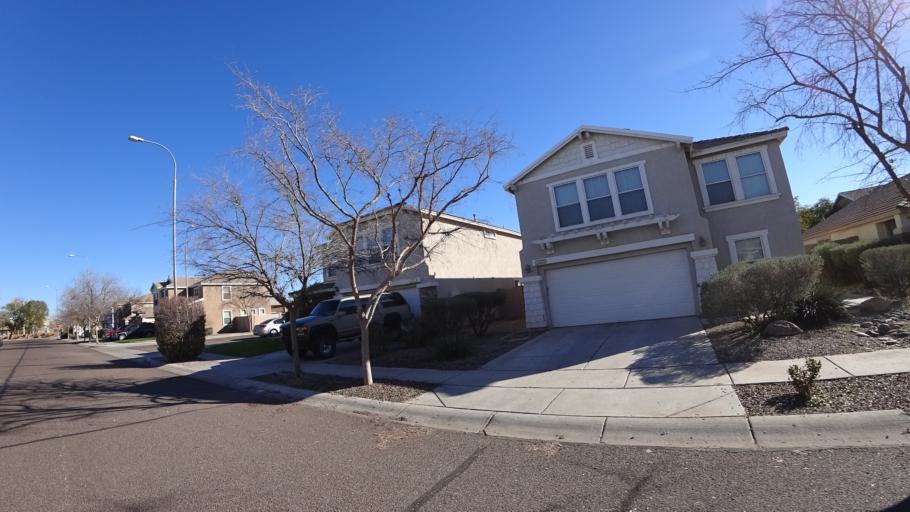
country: US
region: Arizona
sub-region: Maricopa County
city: Avondale
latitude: 33.4332
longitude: -112.3180
